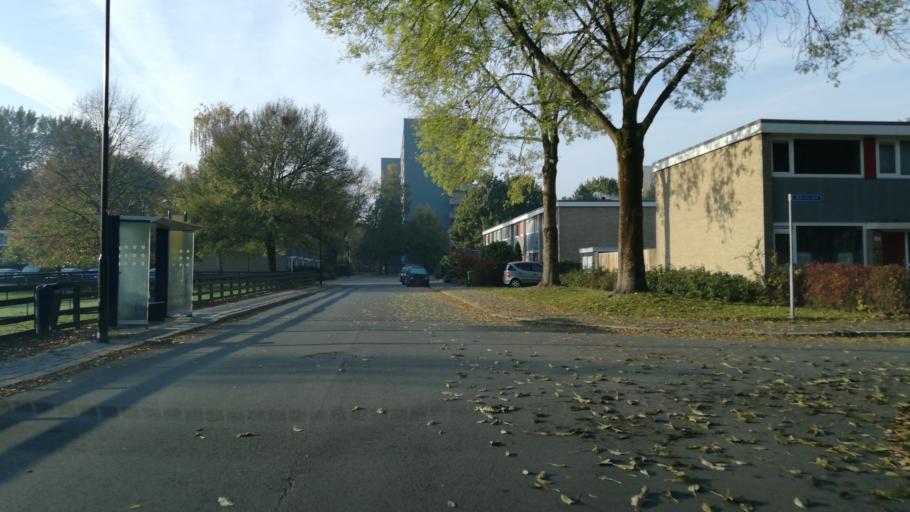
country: NL
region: Gelderland
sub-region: Gemeente Apeldoorn
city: Apeldoorn
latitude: 52.2228
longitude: 6.0019
